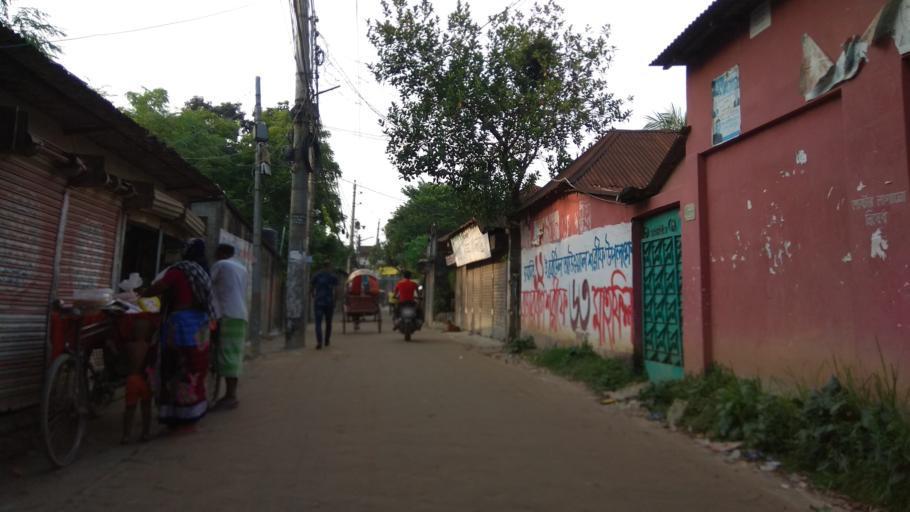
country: BD
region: Dhaka
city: Tungi
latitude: 23.8423
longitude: 90.3873
